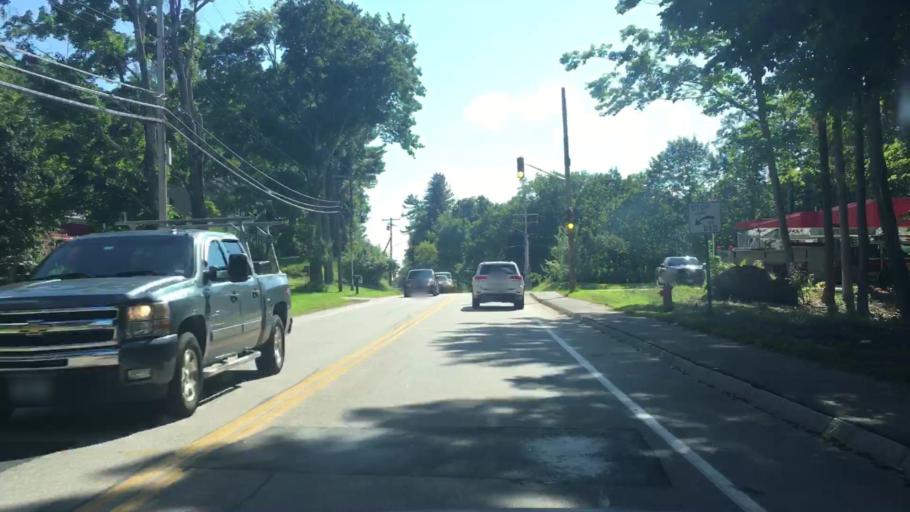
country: US
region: New Hampshire
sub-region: Strafford County
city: Dover
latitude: 43.1784
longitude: -70.8797
